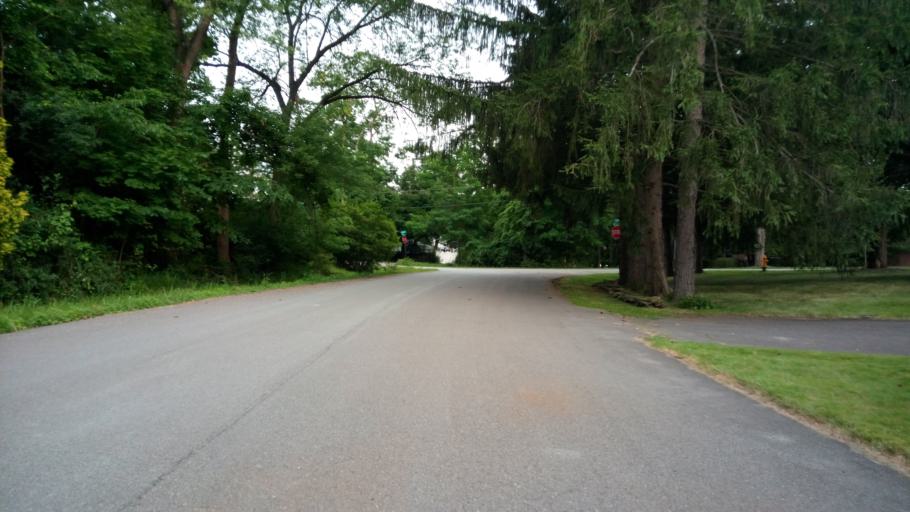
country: US
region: New York
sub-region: Chemung County
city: West Elmira
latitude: 42.0818
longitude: -76.8406
